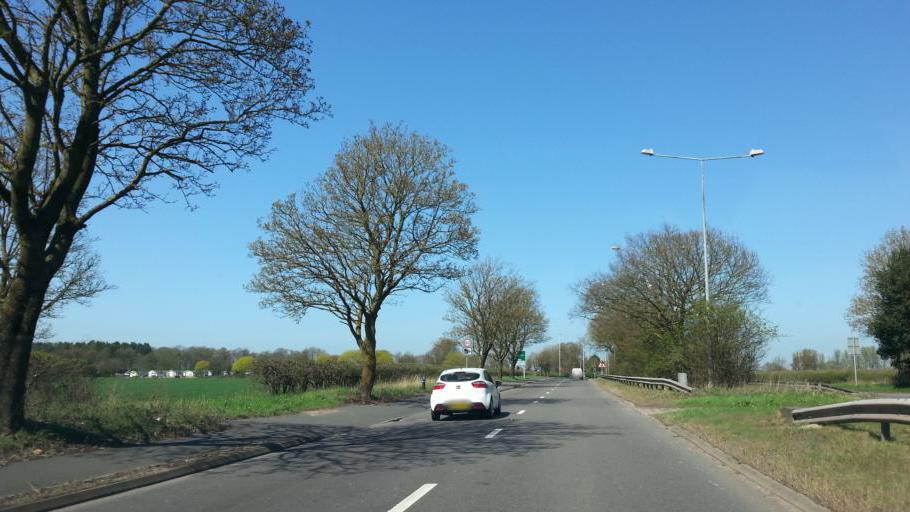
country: GB
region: England
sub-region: Staffordshire
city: Brewood
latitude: 52.6804
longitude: -2.1322
